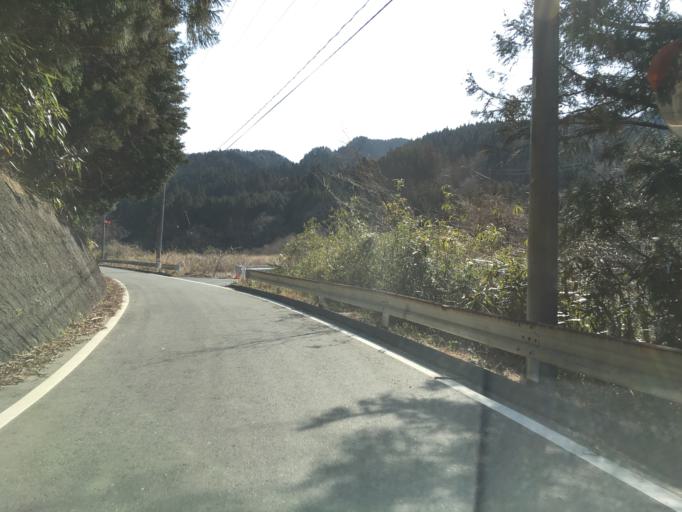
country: JP
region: Ibaraki
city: Kitaibaraki
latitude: 36.7948
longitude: 140.6531
